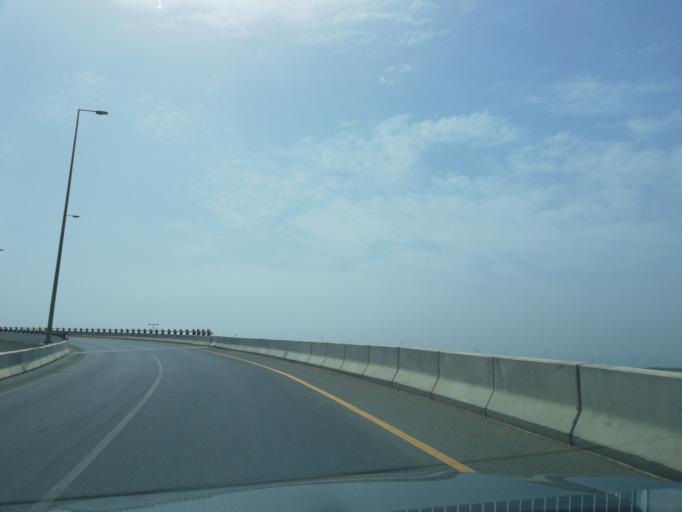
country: OM
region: Muhafazat Masqat
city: Bawshar
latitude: 23.5836
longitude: 58.3352
